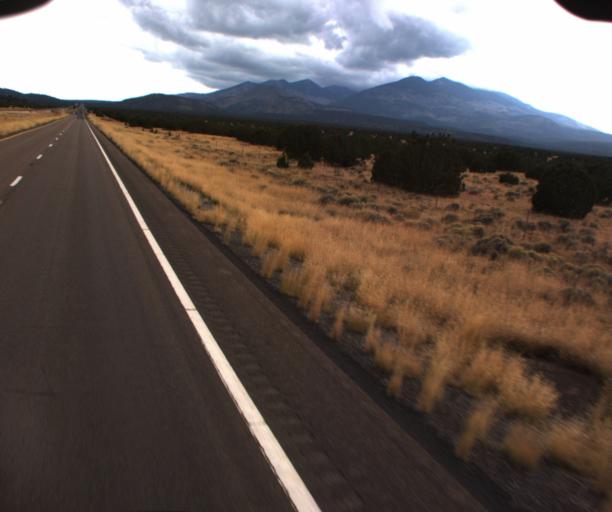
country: US
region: Arizona
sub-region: Coconino County
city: Flagstaff
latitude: 35.4329
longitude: -111.5679
